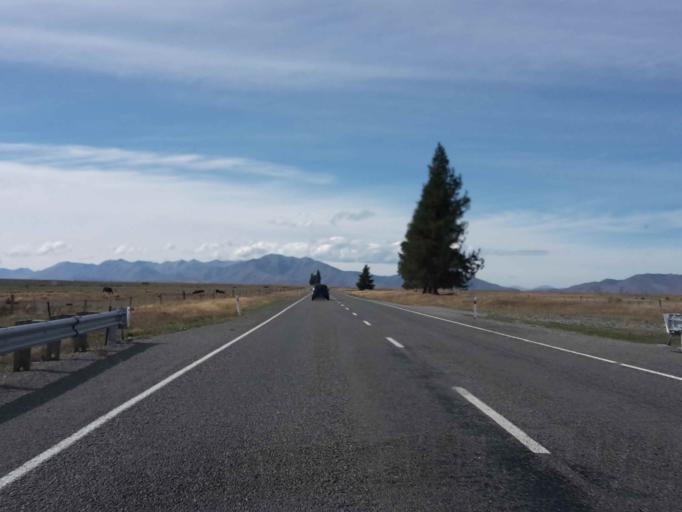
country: NZ
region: Canterbury
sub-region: Timaru District
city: Pleasant Point
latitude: -44.1748
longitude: 170.3231
